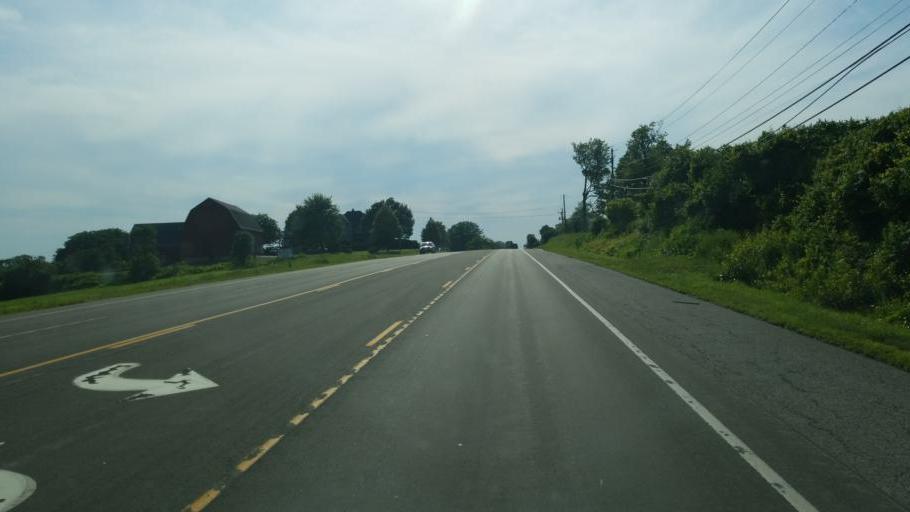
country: US
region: New York
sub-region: Genesee County
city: Batavia
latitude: 42.9873
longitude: -78.1195
